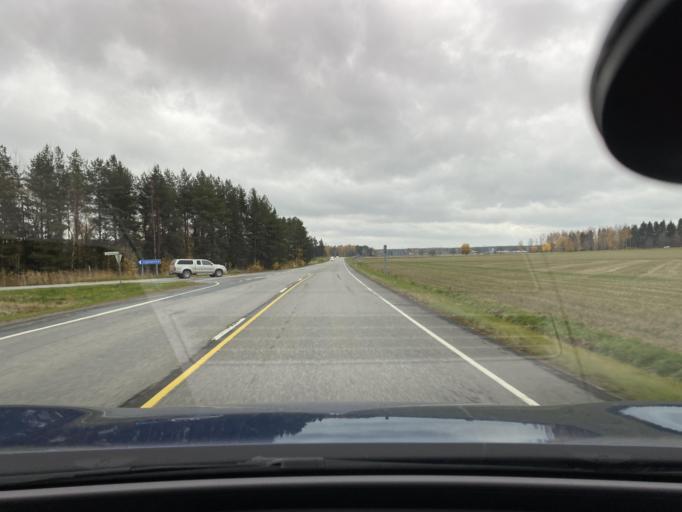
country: FI
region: Satakunta
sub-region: Rauma
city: Kiukainen
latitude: 61.1901
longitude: 22.0603
